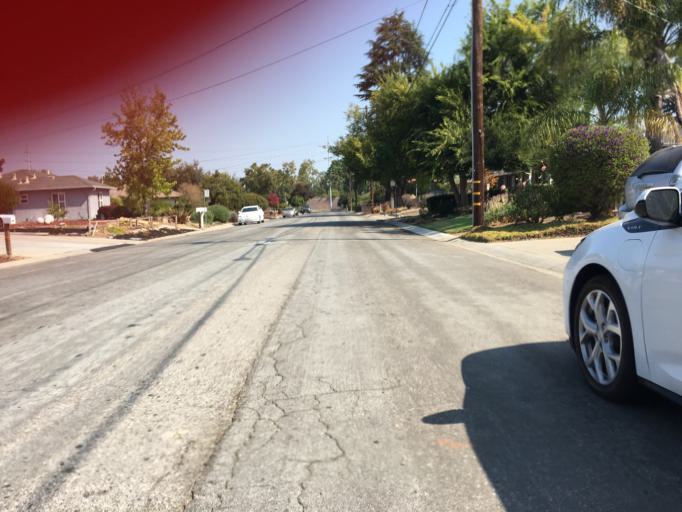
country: US
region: California
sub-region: Santa Clara County
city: Cupertino
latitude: 37.3322
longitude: -122.0261
